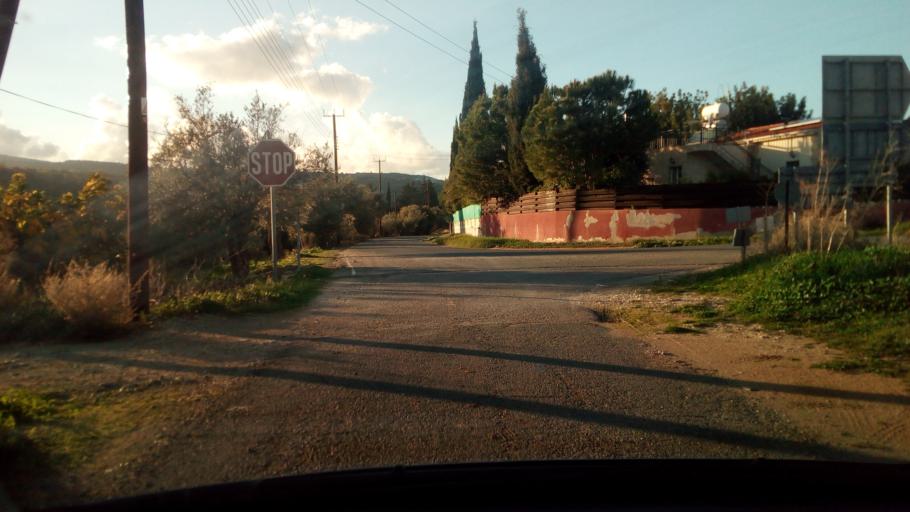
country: CY
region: Pafos
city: Polis
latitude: 34.9789
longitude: 32.4640
